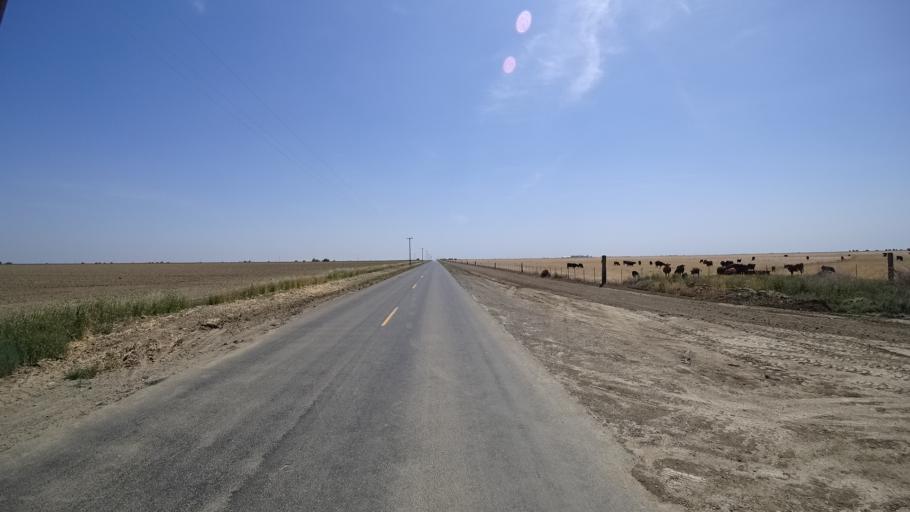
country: US
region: California
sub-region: Kings County
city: Stratford
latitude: 36.1377
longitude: -119.9321
